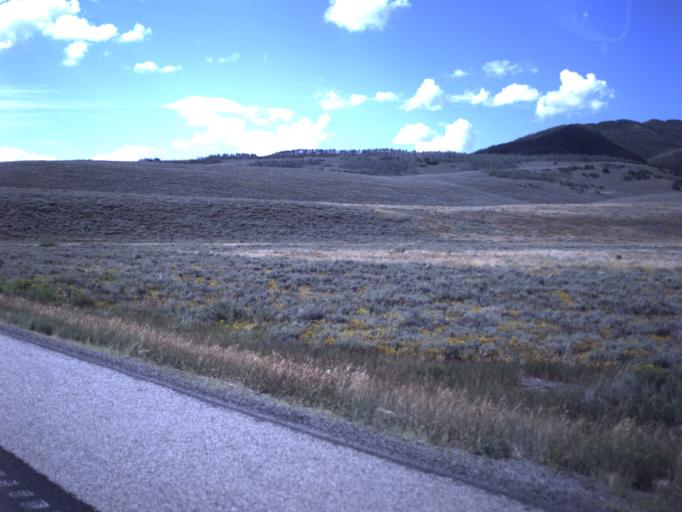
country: US
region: Utah
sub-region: Wasatch County
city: Heber
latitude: 40.2297
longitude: -111.1200
